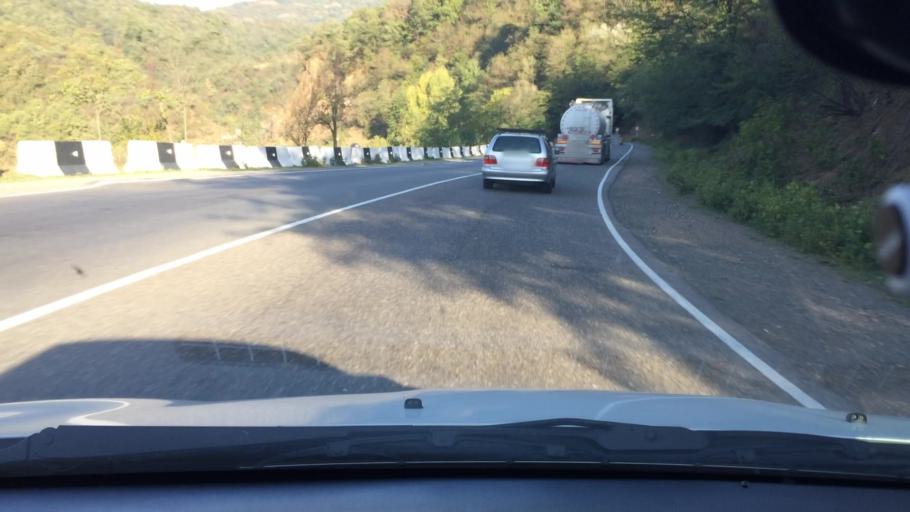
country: GE
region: Imereti
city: Kharagauli
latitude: 42.1013
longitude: 43.2159
